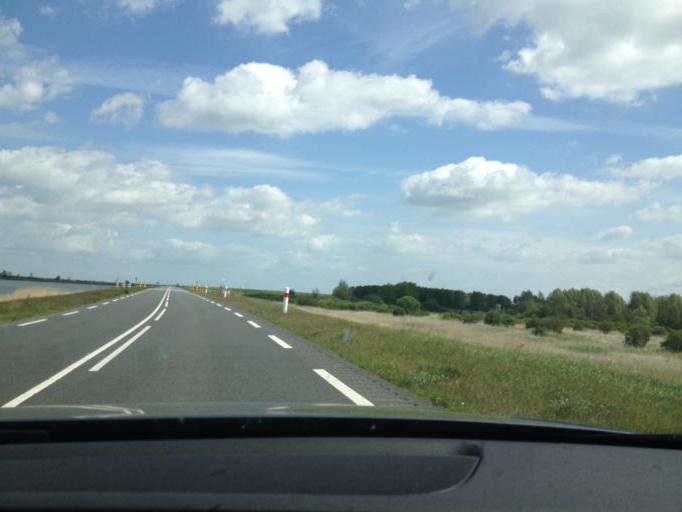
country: NL
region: Flevoland
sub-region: Gemeente Almere
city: Almere Stad
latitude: 52.3937
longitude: 5.1578
